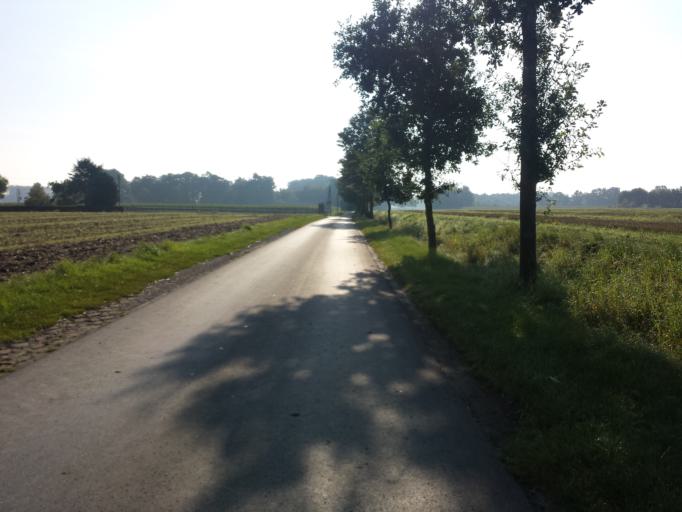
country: DE
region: North Rhine-Westphalia
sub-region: Regierungsbezirk Detmold
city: Harsewinkel
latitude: 51.9414
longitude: 8.3051
